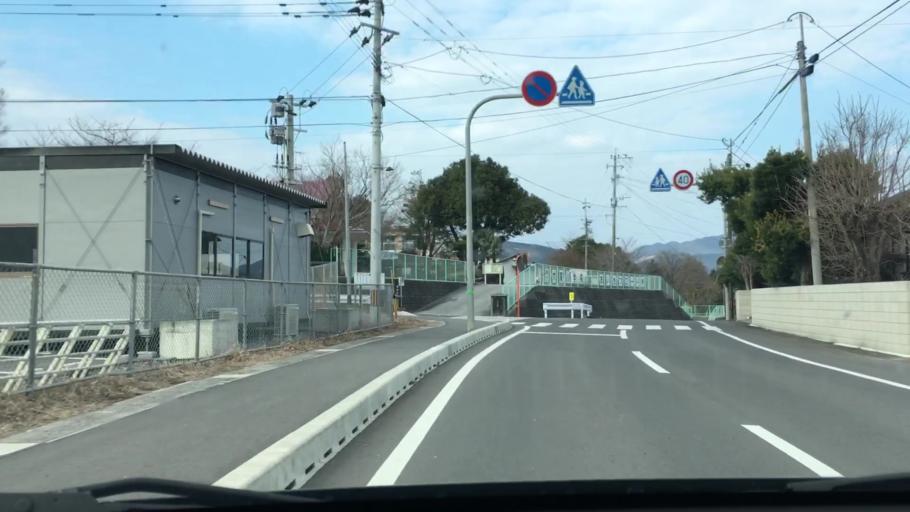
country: JP
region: Miyazaki
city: Kushima
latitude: 31.5243
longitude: 131.2368
